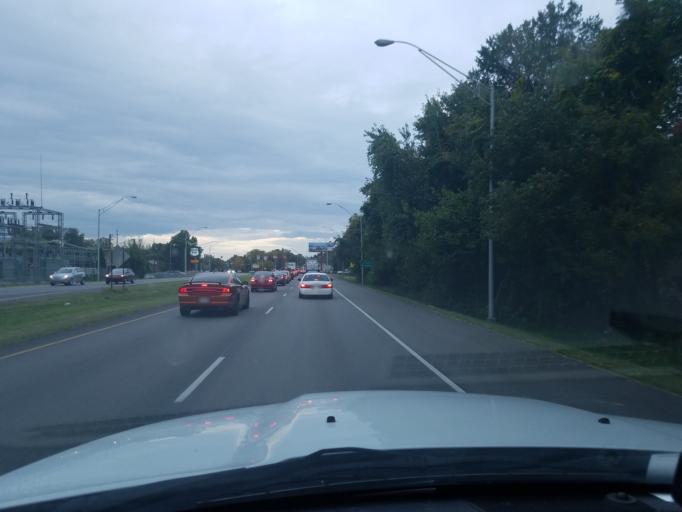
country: US
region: Indiana
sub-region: Vanderburgh County
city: Evansville
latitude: 37.9724
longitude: -87.5440
